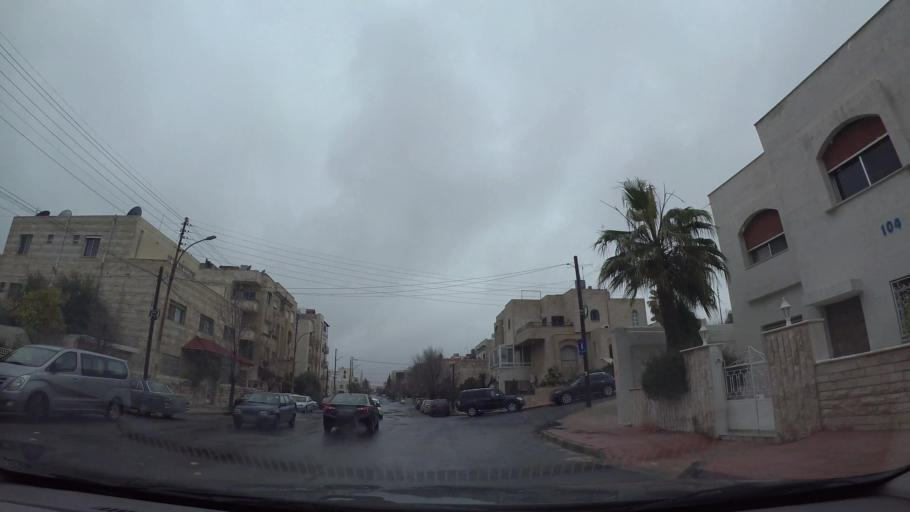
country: JO
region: Amman
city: Wadi as Sir
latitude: 31.9684
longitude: 35.8443
